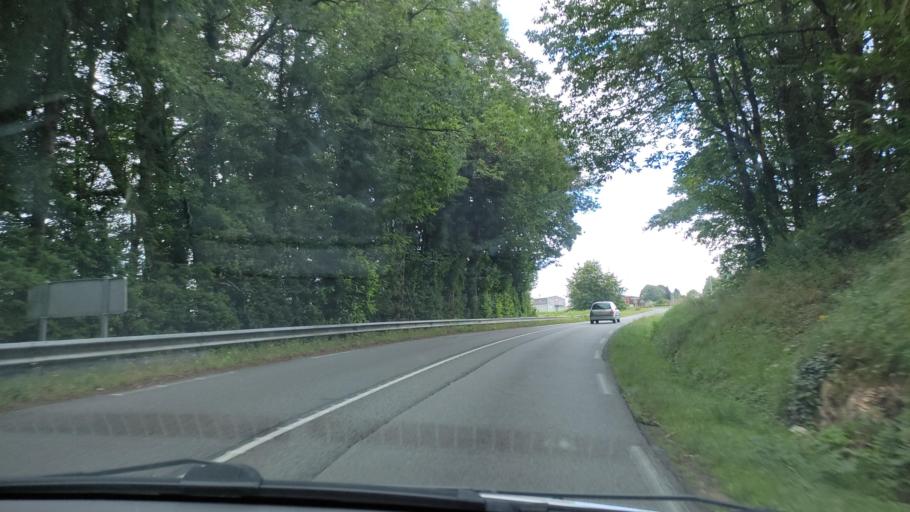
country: FR
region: Limousin
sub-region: Departement de la Haute-Vienne
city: Rilhac-Rancon
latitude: 45.8986
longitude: 1.3079
